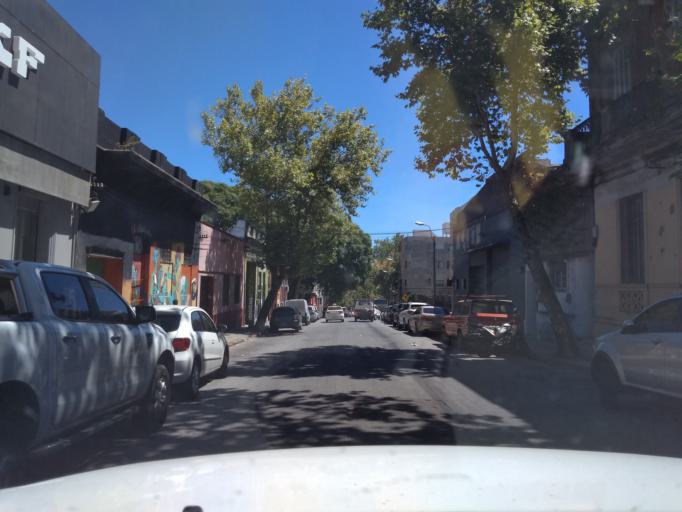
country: UY
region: Montevideo
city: Montevideo
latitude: -34.8971
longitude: -56.1813
